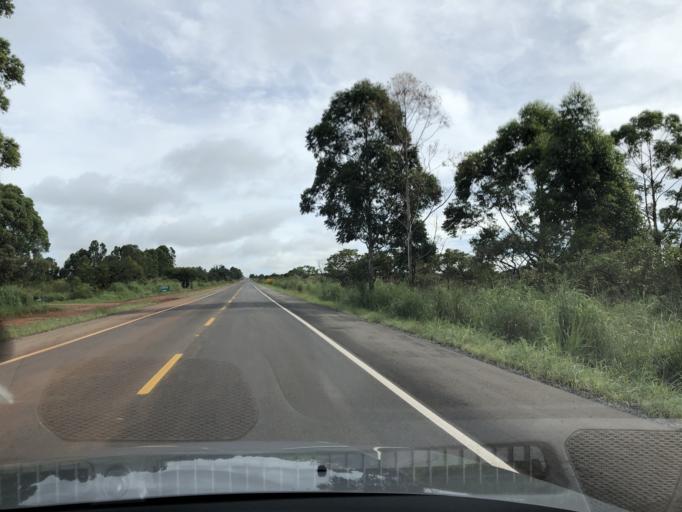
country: BR
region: Federal District
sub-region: Brasilia
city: Brasilia
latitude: -15.6568
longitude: -48.0837
